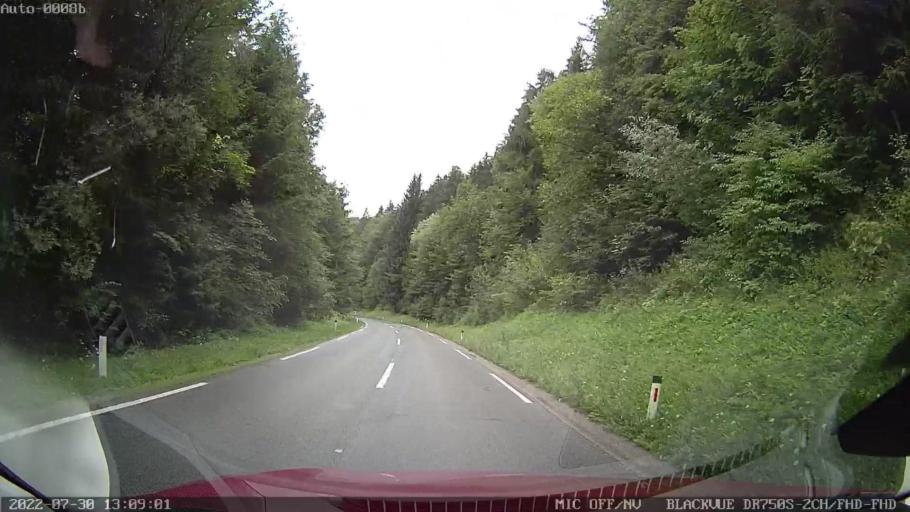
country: SI
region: Dolenjske Toplice
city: Dolenjske Toplice
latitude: 45.6837
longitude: 15.0983
